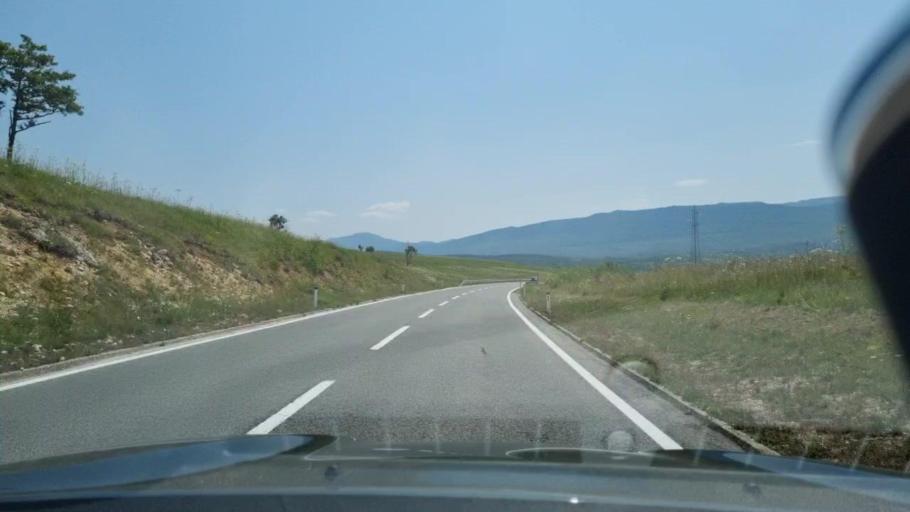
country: BA
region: Federation of Bosnia and Herzegovina
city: Orasac
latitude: 44.5855
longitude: 16.2760
